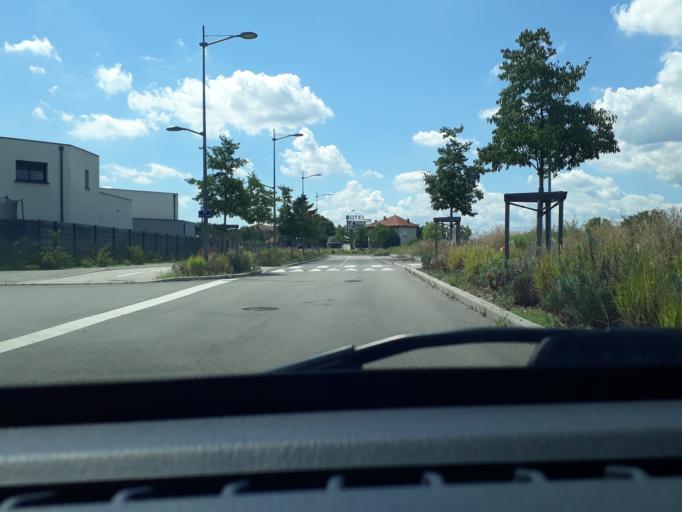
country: FR
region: Rhone-Alpes
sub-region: Departement du Rhone
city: Saint-Priest
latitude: 45.7058
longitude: 4.9175
